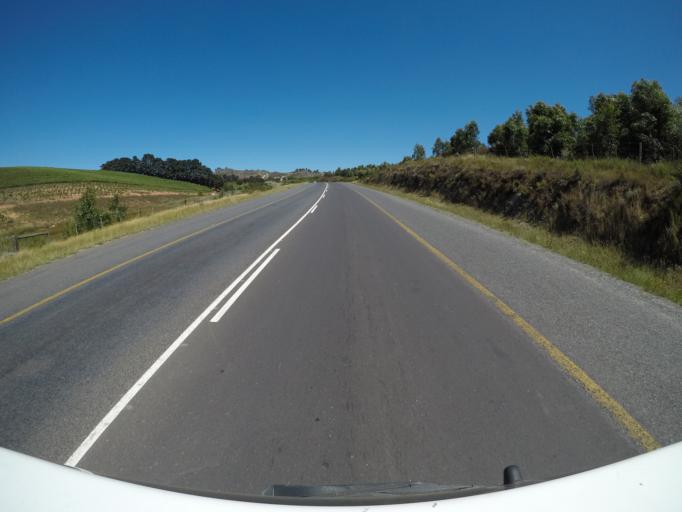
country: ZA
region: Western Cape
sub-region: Overberg District Municipality
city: Grabouw
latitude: -34.1631
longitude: 19.0181
